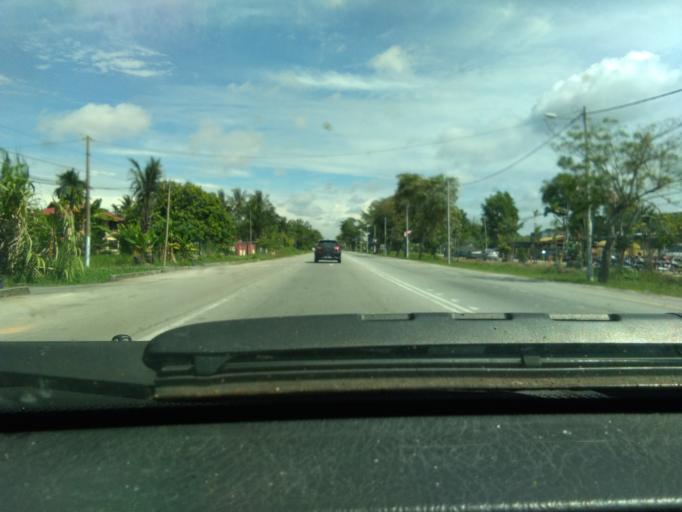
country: MY
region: Perak
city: Parit Buntar
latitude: 5.1046
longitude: 100.4855
